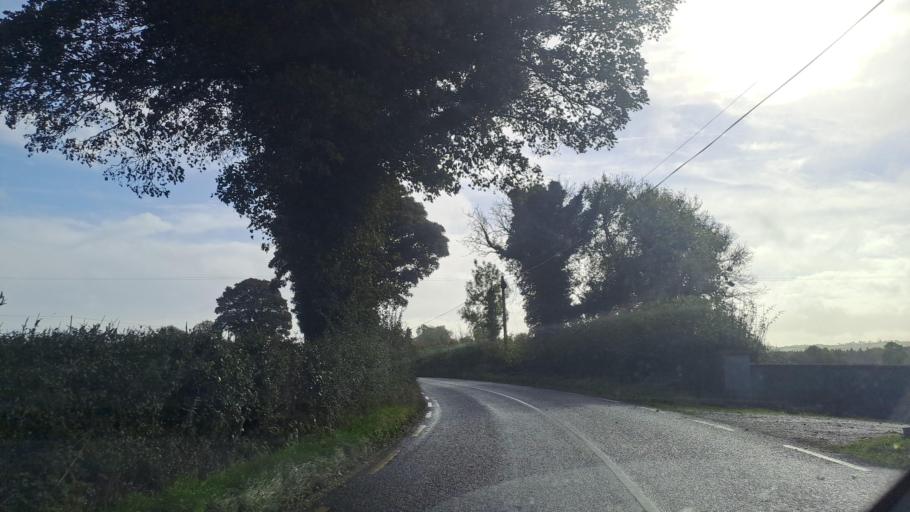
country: IE
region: Ulster
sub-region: County Monaghan
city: Carrickmacross
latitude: 53.9193
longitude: -6.7123
